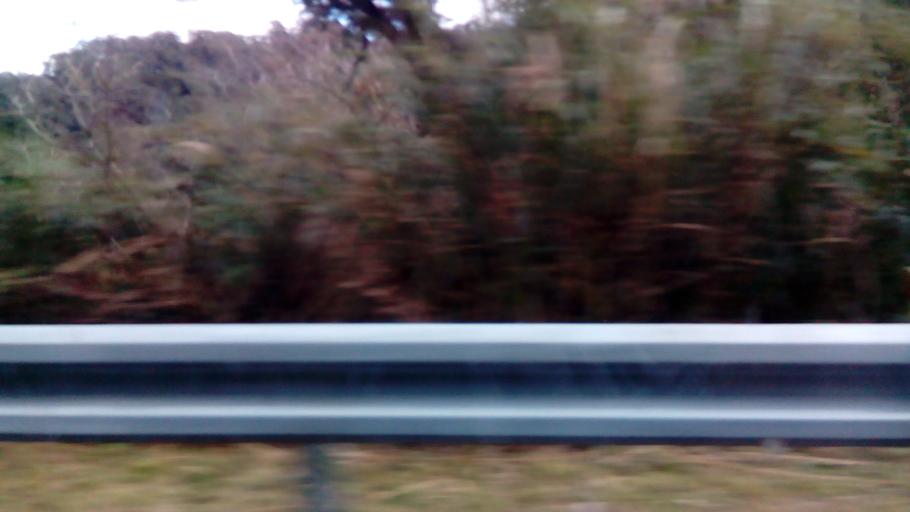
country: TW
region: Taiwan
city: Daxi
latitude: 24.4052
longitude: 121.3638
